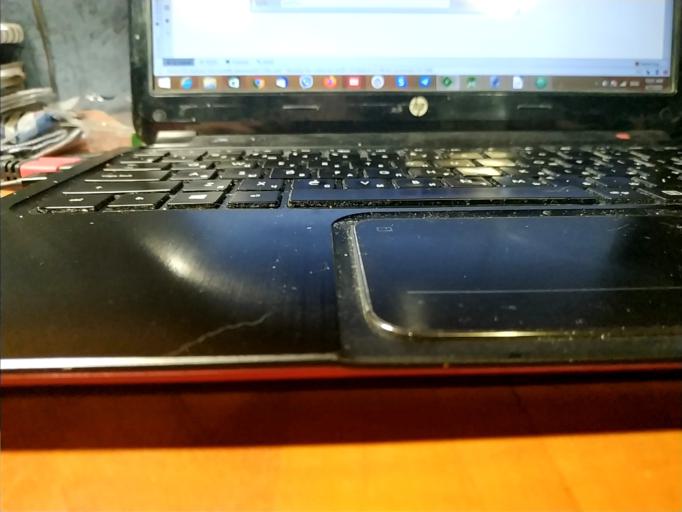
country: RU
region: Vologda
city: Suda
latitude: 58.9167
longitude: 37.5432
